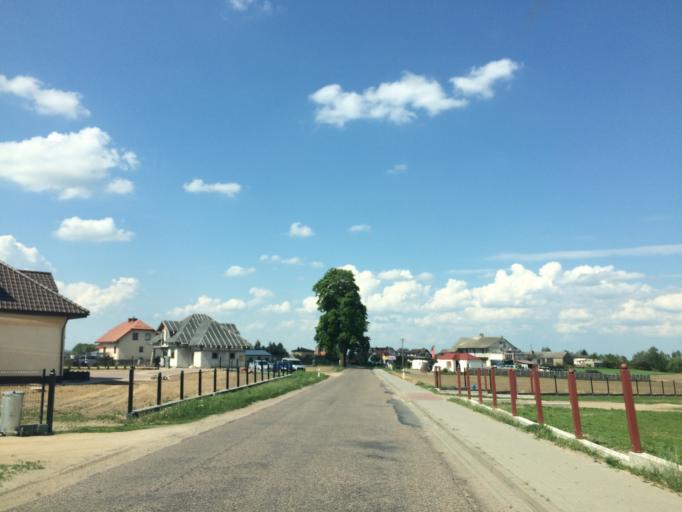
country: PL
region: Warmian-Masurian Voivodeship
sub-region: Powiat ilawski
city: Lubawa
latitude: 53.4114
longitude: 19.7718
